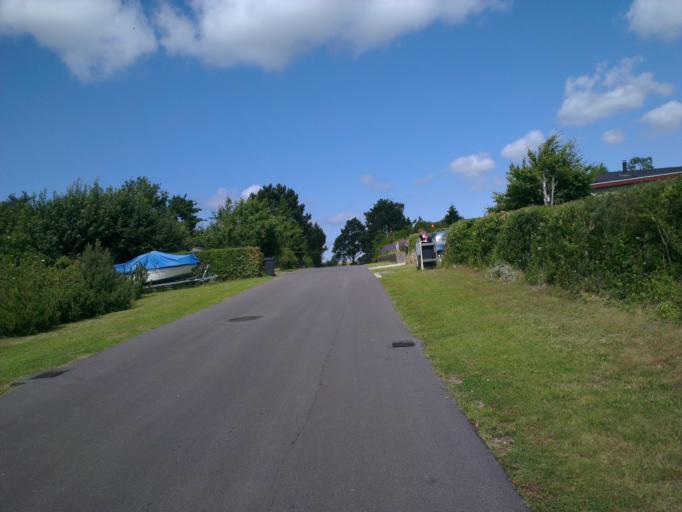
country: DK
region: Zealand
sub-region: Lejre Kommune
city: Ejby
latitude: 55.7495
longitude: 11.8640
